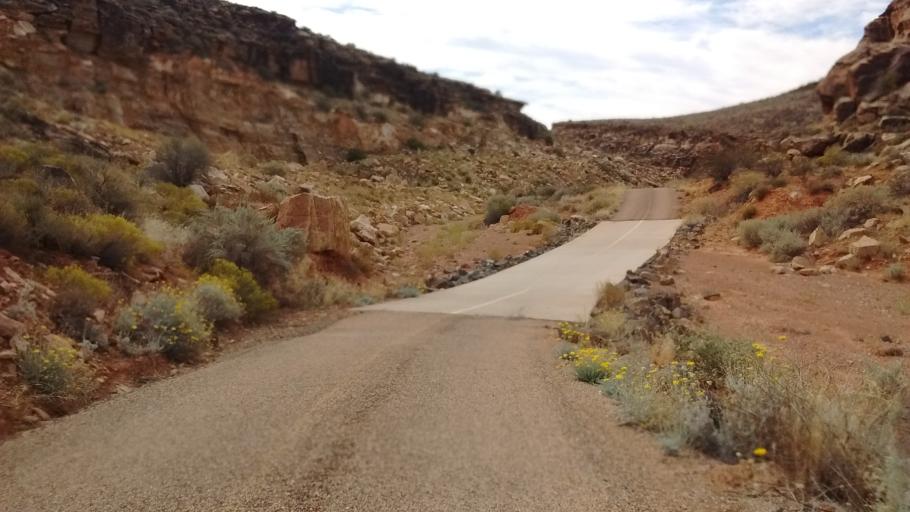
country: US
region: Utah
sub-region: Washington County
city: Washington
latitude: 37.1310
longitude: -113.4706
